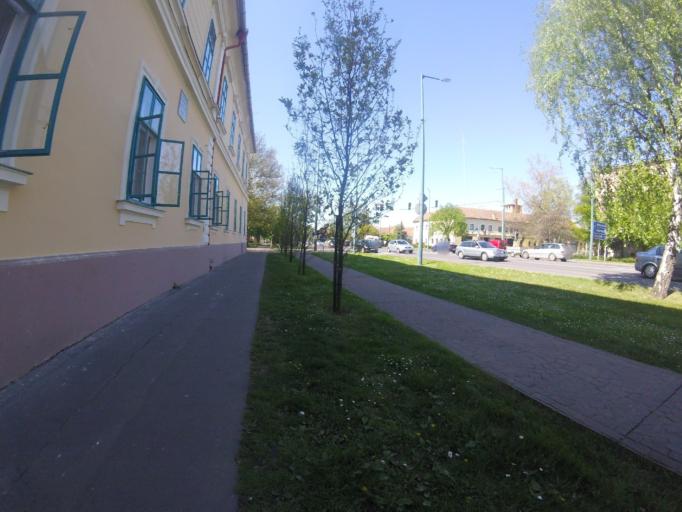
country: HU
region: Bekes
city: Gyula
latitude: 46.6425
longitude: 21.2694
